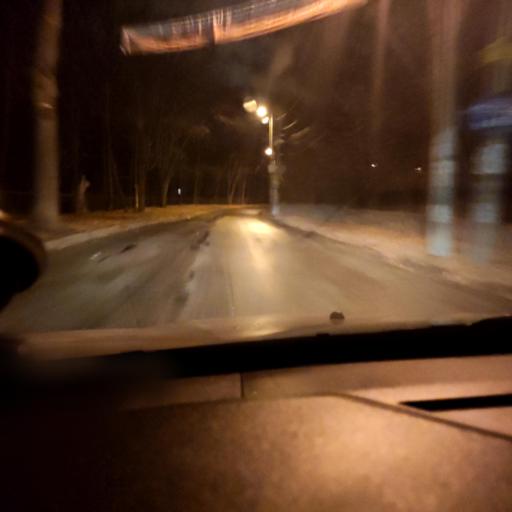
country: RU
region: Samara
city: Samara
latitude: 53.2888
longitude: 50.1977
